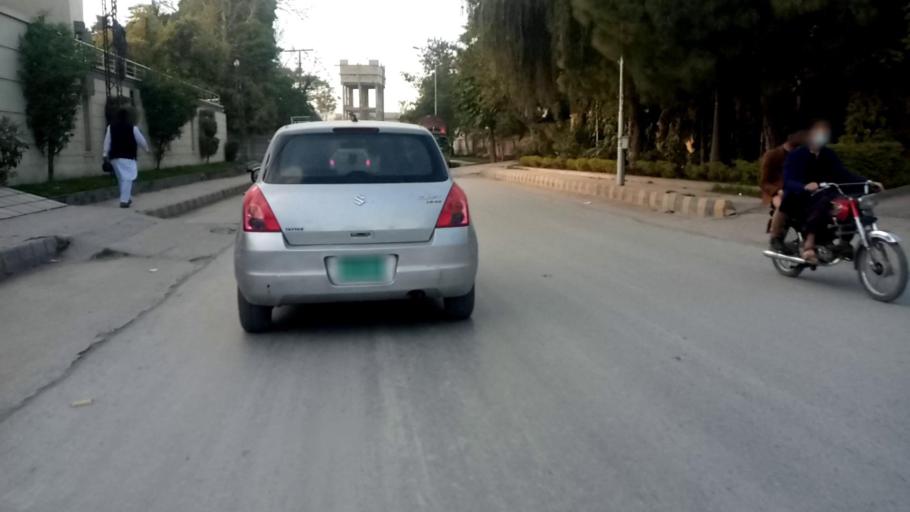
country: PK
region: Khyber Pakhtunkhwa
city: Peshawar
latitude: 34.0188
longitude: 71.5545
